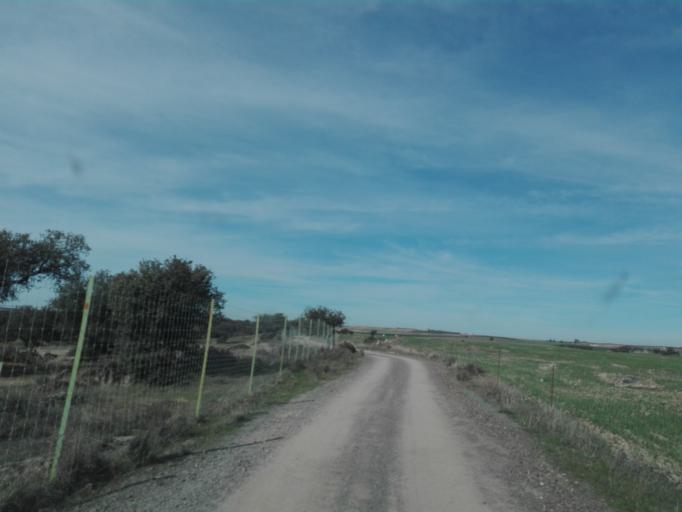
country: ES
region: Extremadura
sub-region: Provincia de Badajoz
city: Azuaga
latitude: 38.2328
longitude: -5.7420
